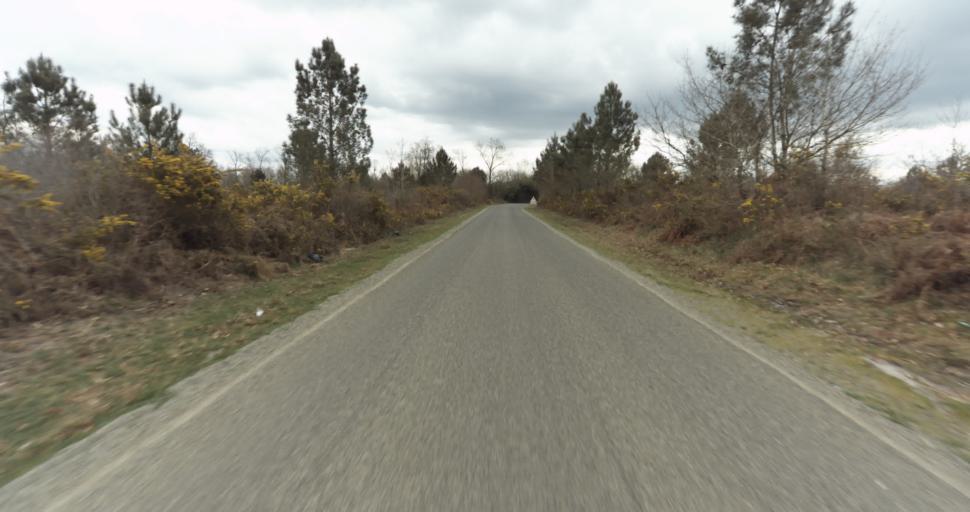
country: FR
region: Aquitaine
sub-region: Departement des Landes
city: Roquefort
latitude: 44.0168
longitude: -0.3427
